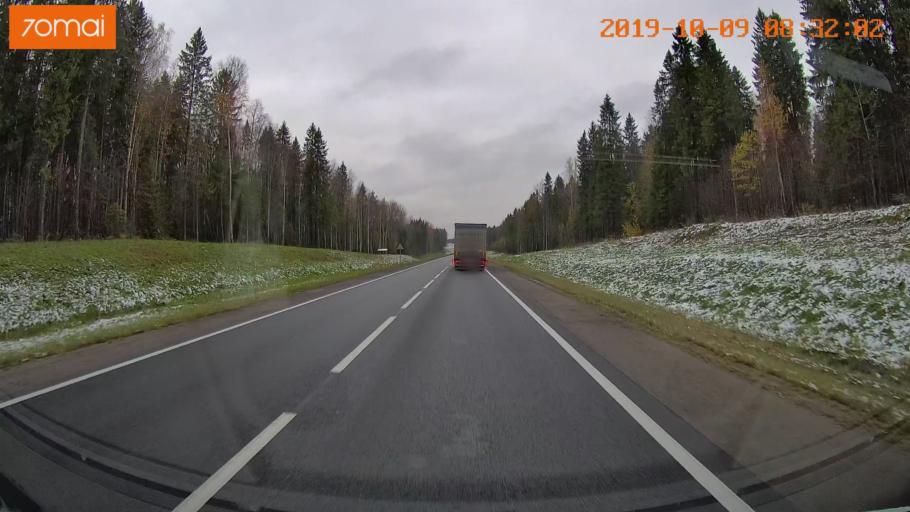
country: RU
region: Vologda
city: Gryazovets
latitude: 58.8615
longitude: 40.1987
